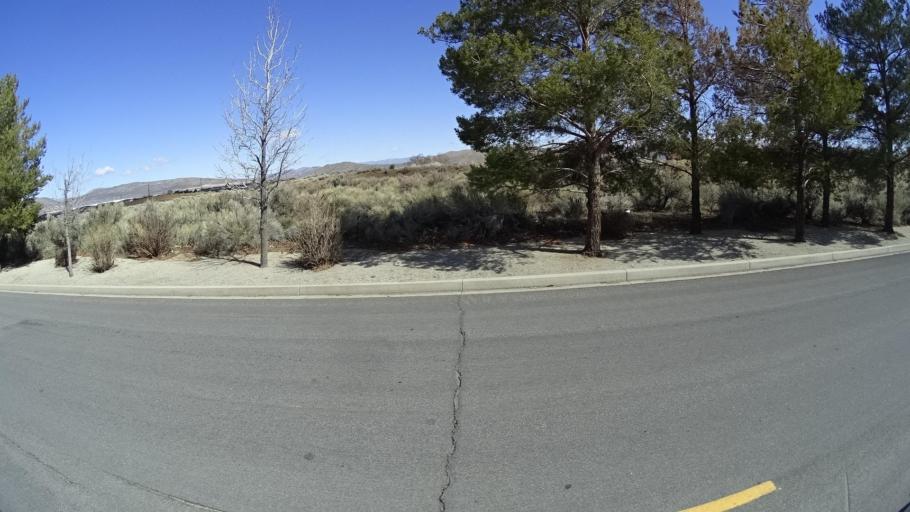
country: US
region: Nevada
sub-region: Washoe County
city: Lemmon Valley
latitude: 39.6338
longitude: -119.8656
